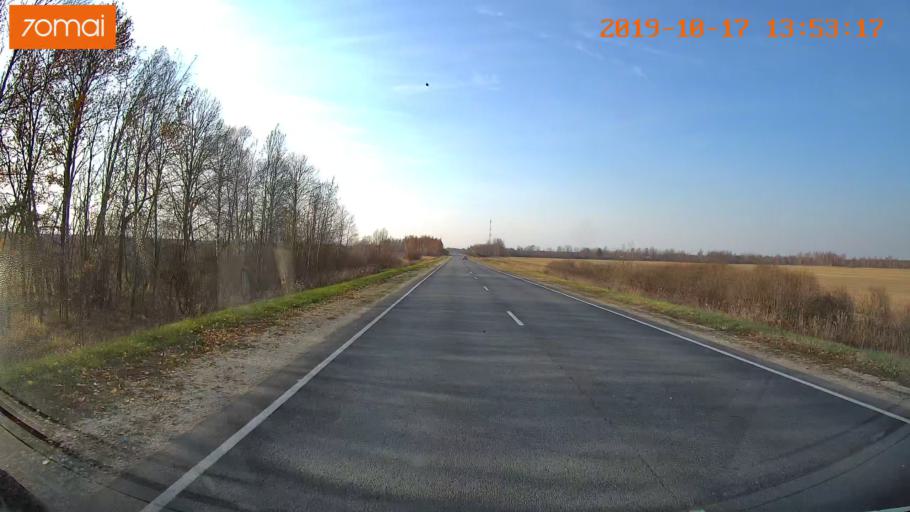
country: RU
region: Rjazan
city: Spas-Klepiki
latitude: 55.1419
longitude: 40.3453
